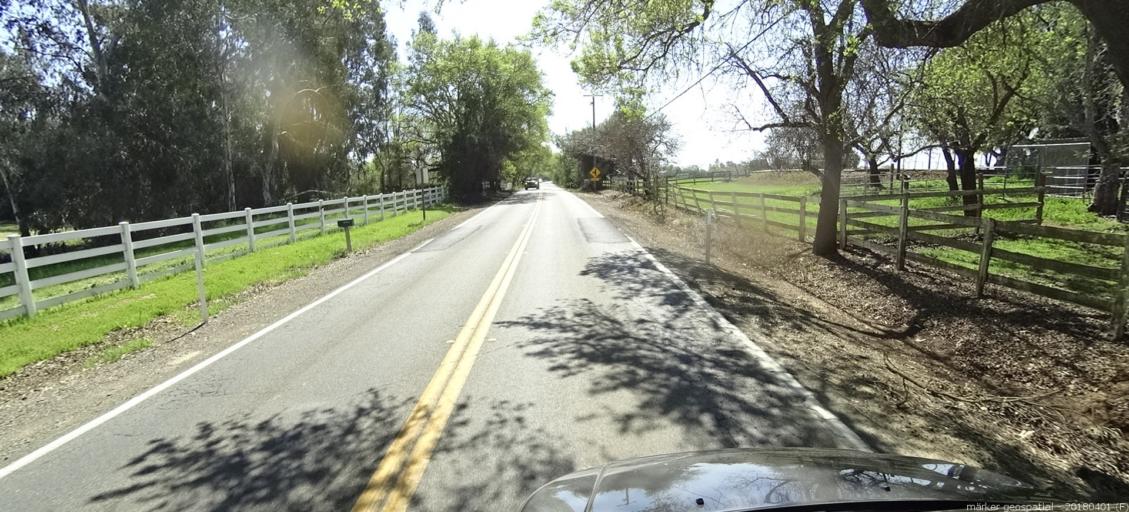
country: US
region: California
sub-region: Sacramento County
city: Wilton
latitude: 38.4171
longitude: -121.2535
